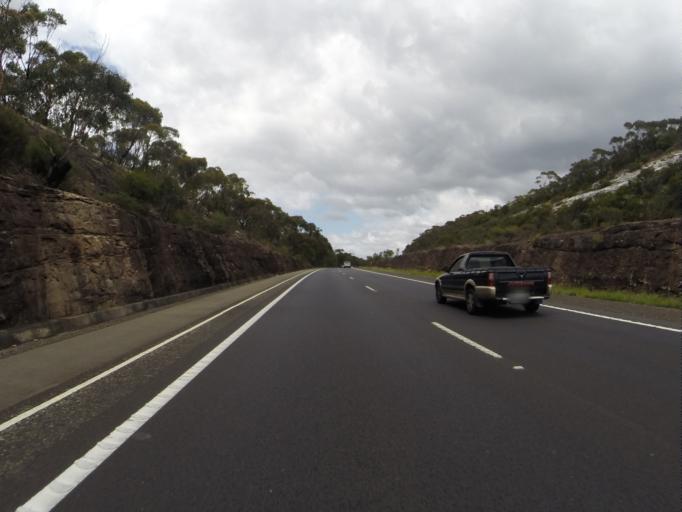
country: AU
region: New South Wales
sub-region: Wollongong
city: Helensburgh
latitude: -34.1744
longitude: 150.9777
